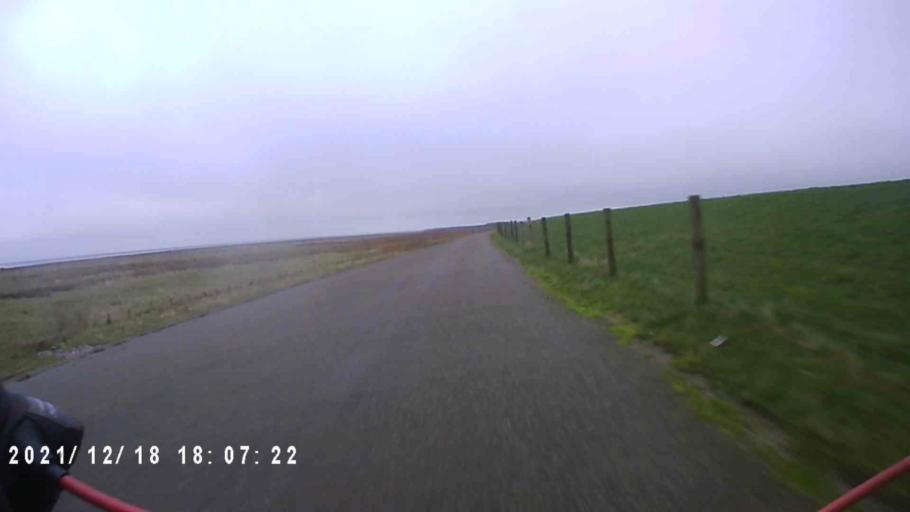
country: NL
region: Friesland
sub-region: Gemeente Dongeradeel
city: Holwerd
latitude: 53.3851
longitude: 5.9175
